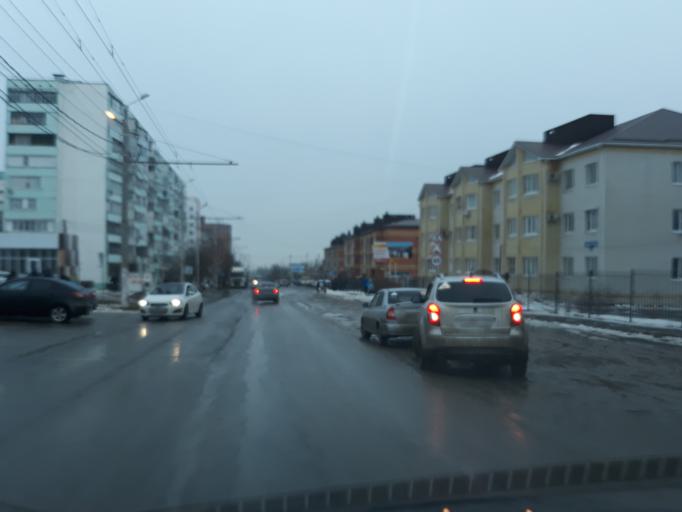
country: RU
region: Rostov
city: Taganrog
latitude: 47.2790
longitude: 38.9242
